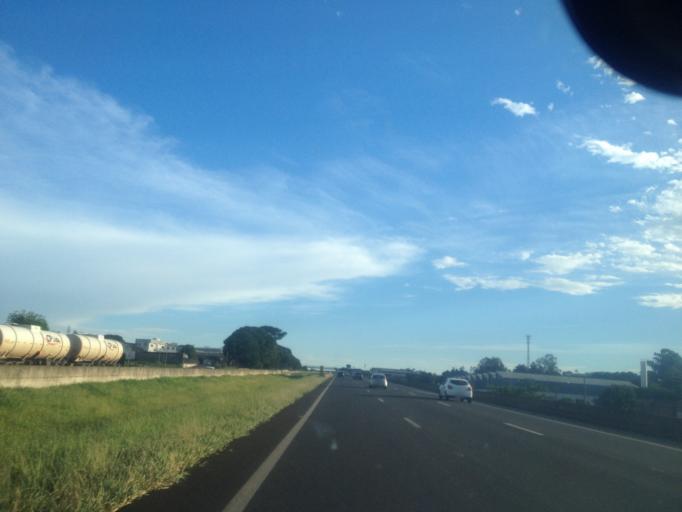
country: BR
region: Sao Paulo
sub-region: Araras
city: Araras
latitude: -22.3644
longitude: -47.3948
